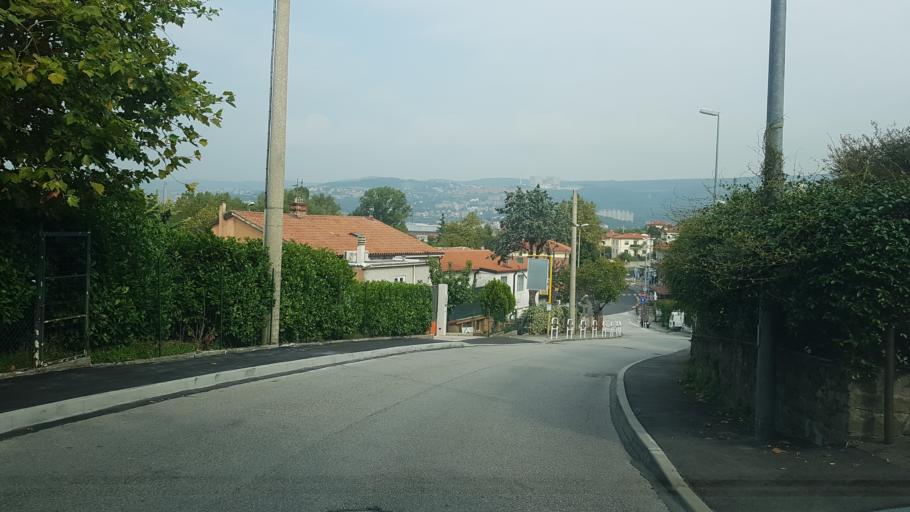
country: IT
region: Friuli Venezia Giulia
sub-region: Provincia di Trieste
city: Domio
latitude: 45.6041
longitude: 13.8066
